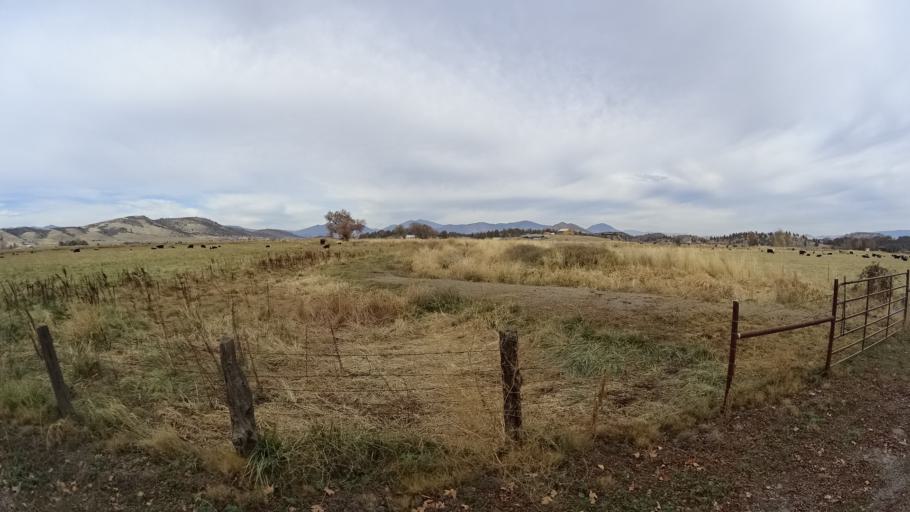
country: US
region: California
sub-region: Siskiyou County
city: Montague
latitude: 41.6603
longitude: -122.5078
